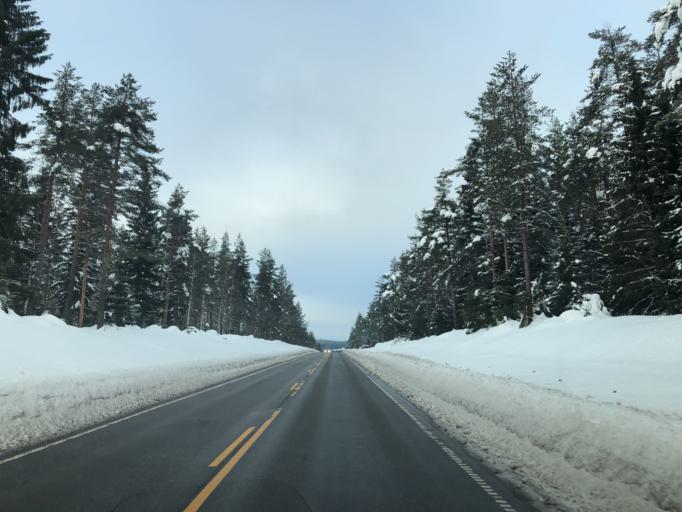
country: NO
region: Hedmark
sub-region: Trysil
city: Innbygda
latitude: 61.2081
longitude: 12.2238
